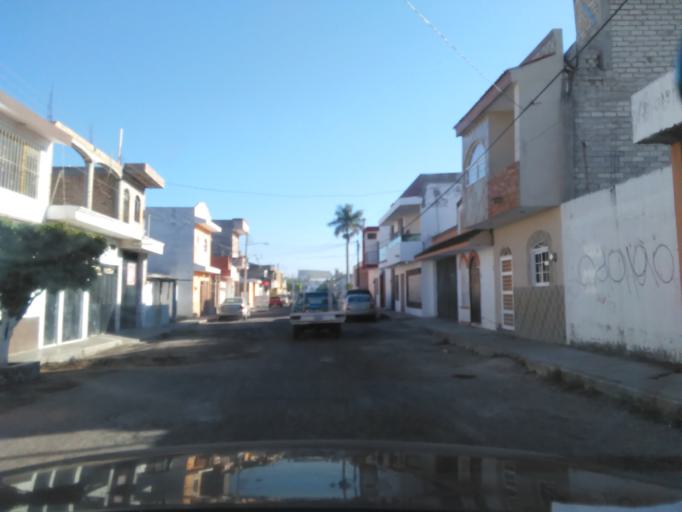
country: MX
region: Nayarit
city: Tepic
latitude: 21.5222
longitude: -104.9024
